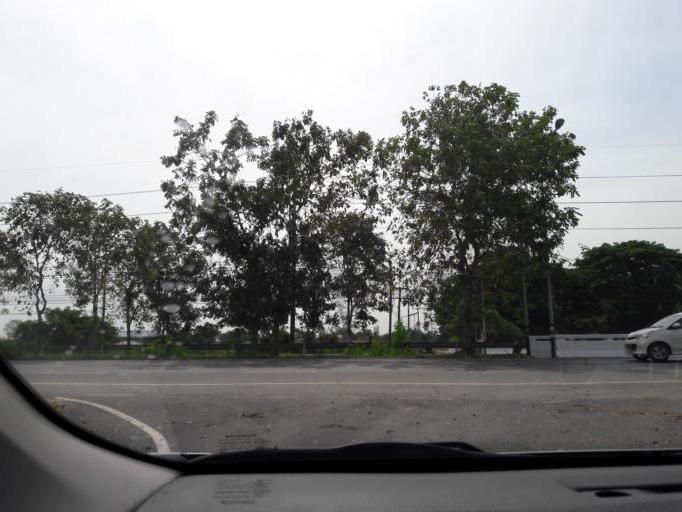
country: TH
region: Ang Thong
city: Ang Thong
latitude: 14.5774
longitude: 100.4547
